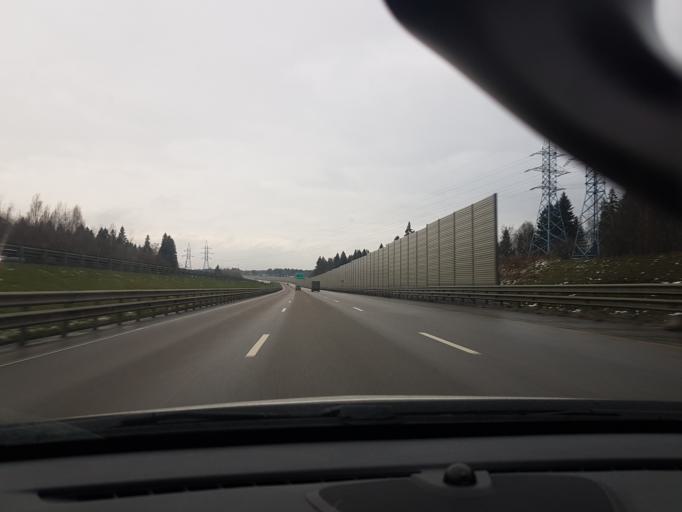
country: RU
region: Moskovskaya
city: Novopetrovskoye
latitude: 55.9702
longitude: 36.4910
